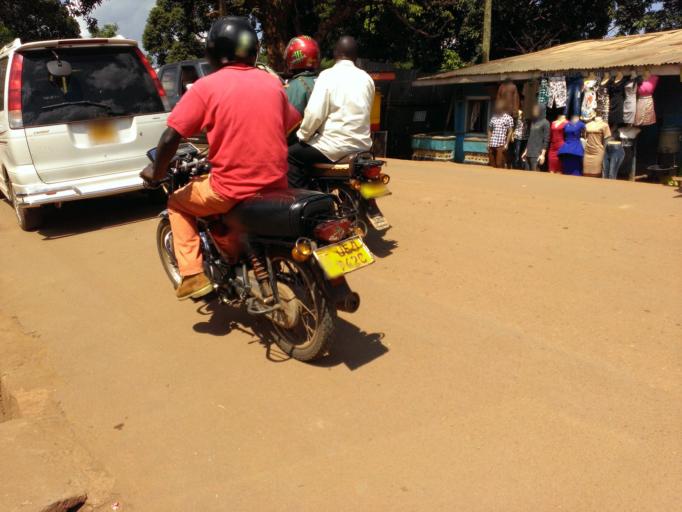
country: UG
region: Central Region
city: Kampala Central Division
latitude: 0.3254
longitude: 32.5680
